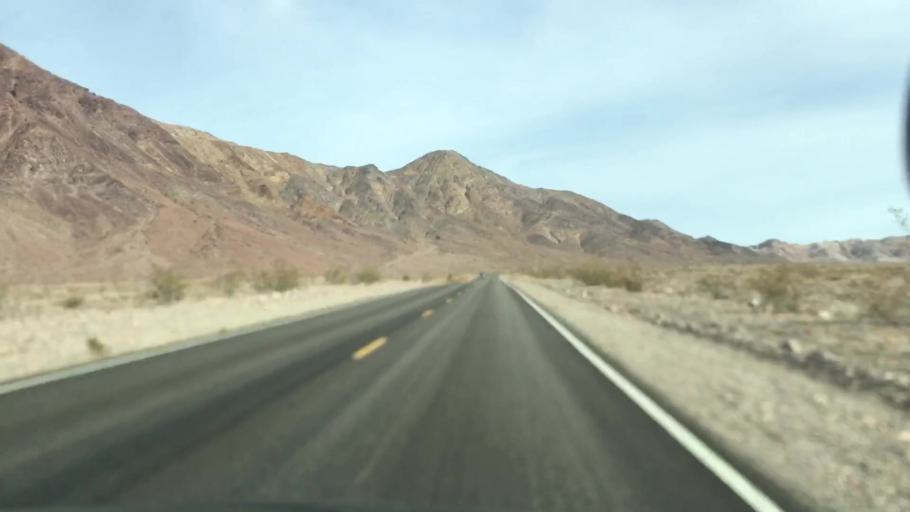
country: US
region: Nevada
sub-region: Nye County
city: Beatty
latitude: 36.6979
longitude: -116.9999
